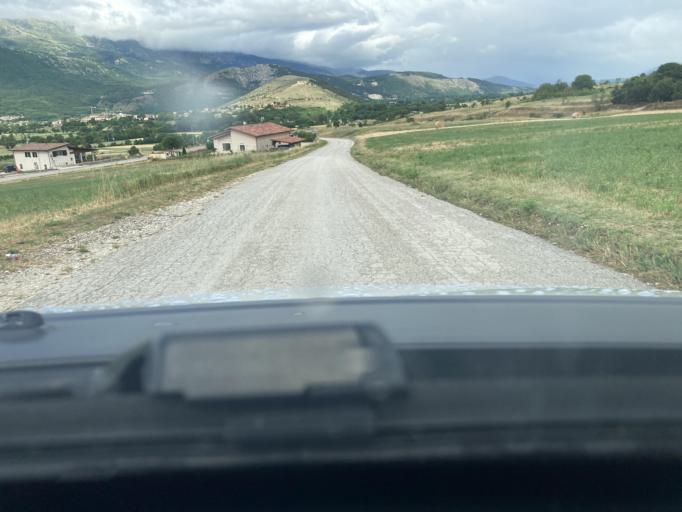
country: IT
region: Abruzzo
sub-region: Provincia dell' Aquila
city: San Demetrio Ne' Vestini
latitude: 42.2934
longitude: 13.5466
